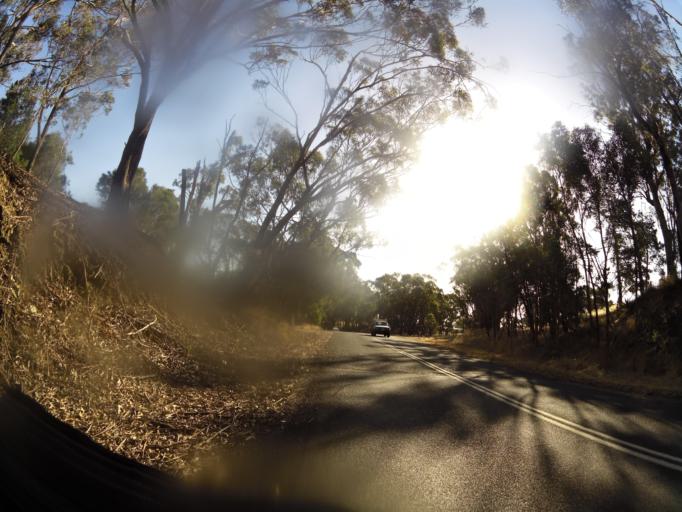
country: AU
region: Victoria
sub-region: Murrindindi
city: Kinglake West
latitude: -37.0216
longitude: 145.1049
